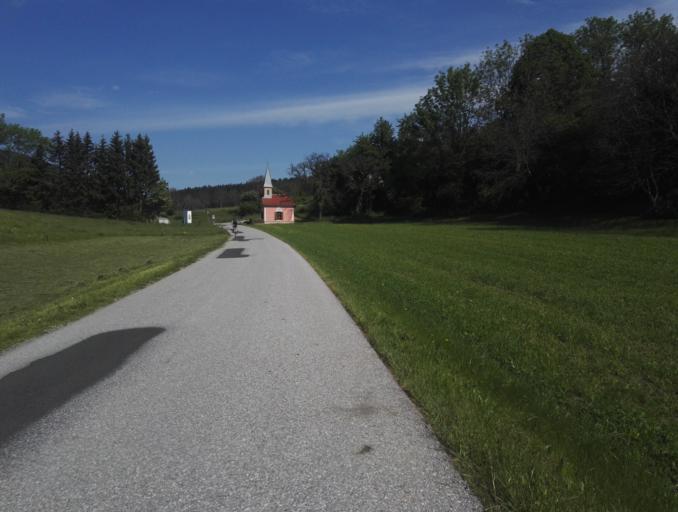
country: AT
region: Styria
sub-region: Politischer Bezirk Graz-Umgebung
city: Stattegg
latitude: 47.1593
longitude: 15.4329
